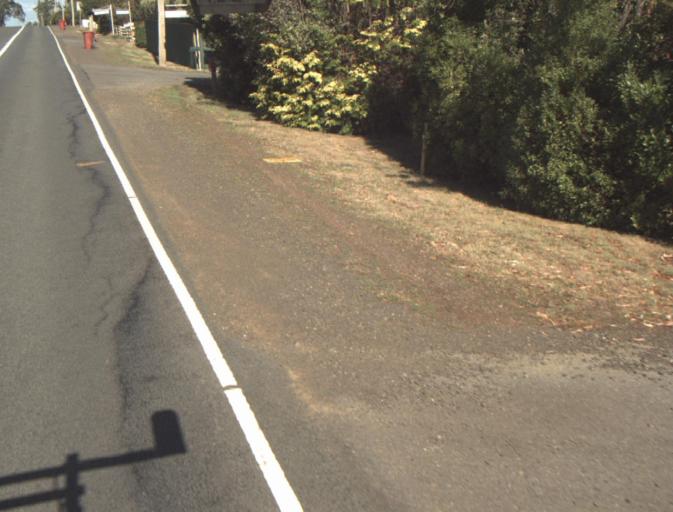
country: AU
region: Tasmania
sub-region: Launceston
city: Mayfield
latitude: -41.3361
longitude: 147.0800
